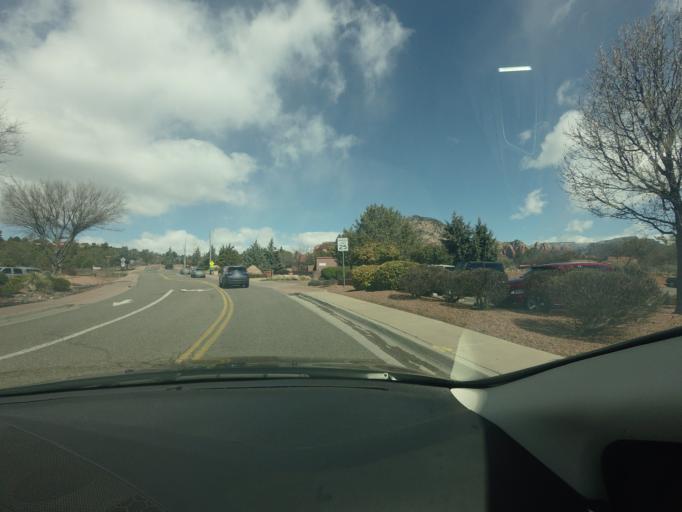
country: US
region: Arizona
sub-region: Yavapai County
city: West Sedona
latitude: 34.8619
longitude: -111.8160
